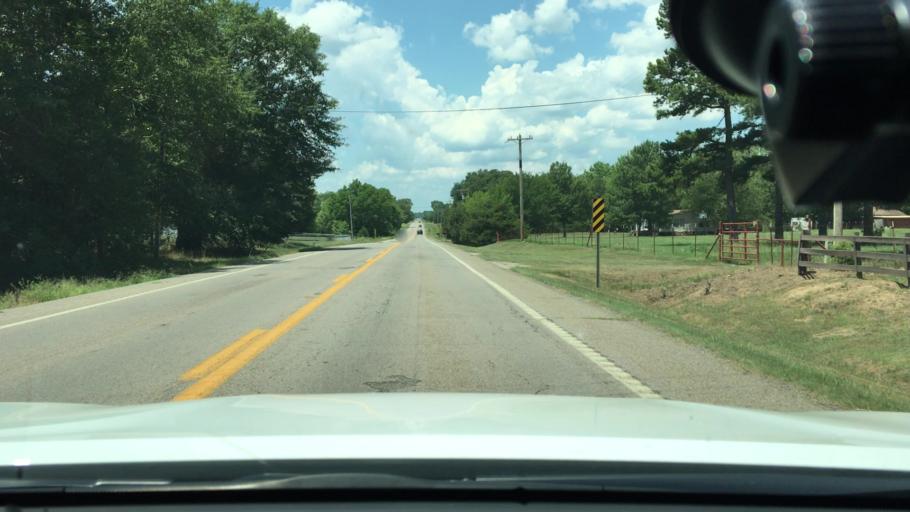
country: US
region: Arkansas
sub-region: Logan County
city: Booneville
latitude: 35.1475
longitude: -93.8458
